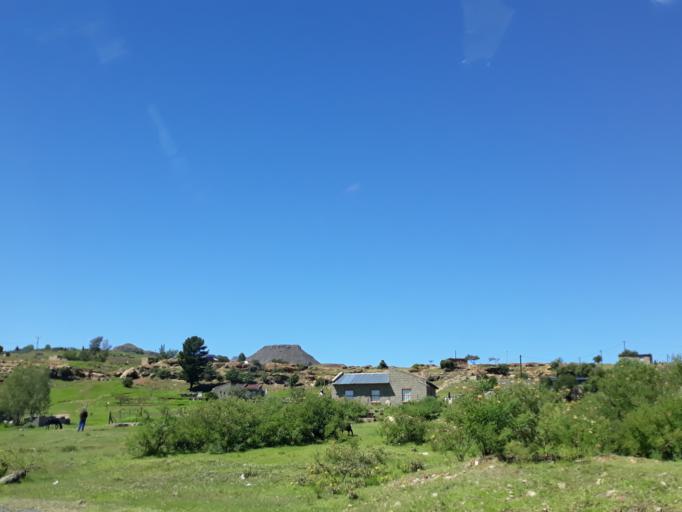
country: LS
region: Mohale's Hoek District
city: Mohale's Hoek
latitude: -30.1070
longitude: 27.4748
